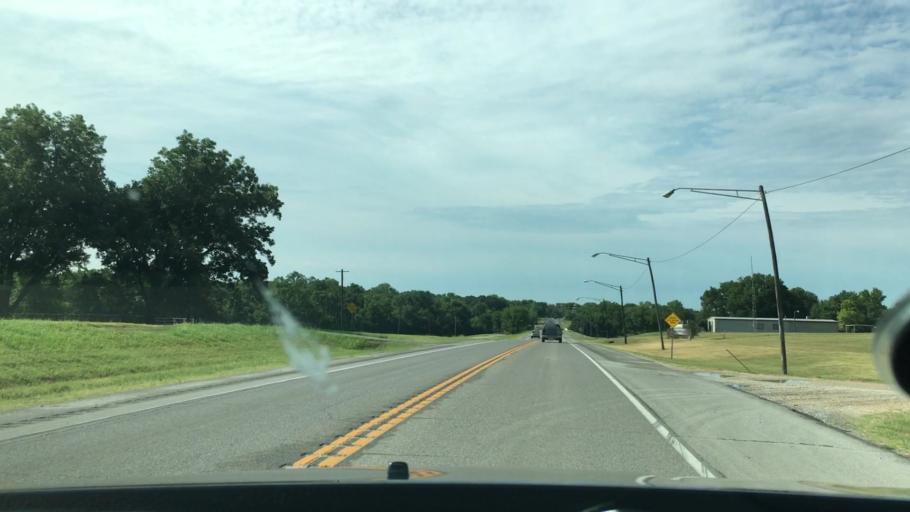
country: US
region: Oklahoma
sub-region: Murray County
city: Sulphur
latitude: 34.5199
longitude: -96.9689
